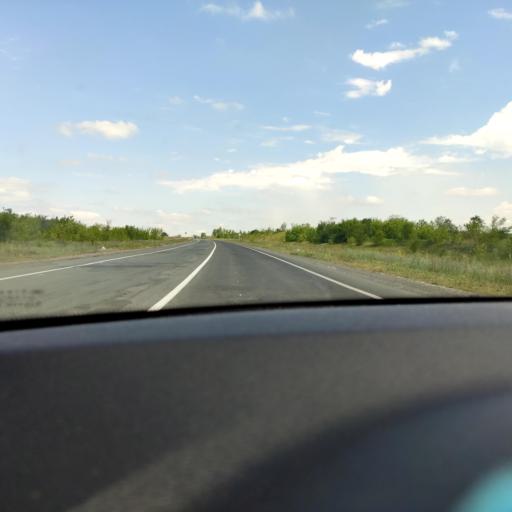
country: RU
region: Samara
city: Petra-Dubrava
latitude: 53.3104
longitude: 50.4216
